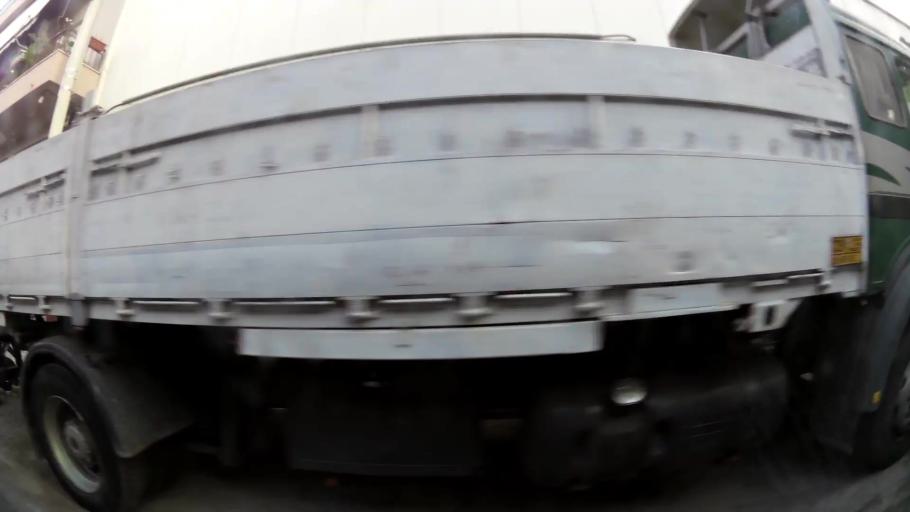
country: GR
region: Attica
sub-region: Nomos Attikis
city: Piraeus
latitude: 37.9533
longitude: 23.6368
